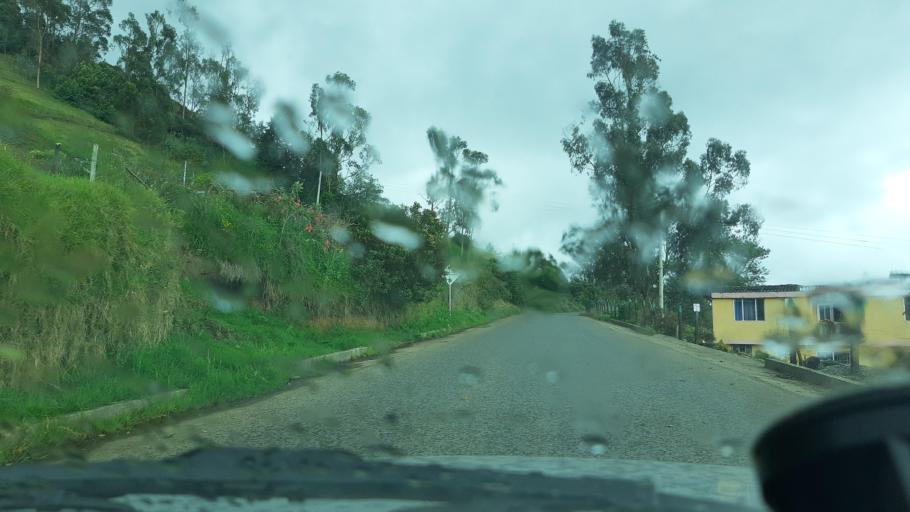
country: CO
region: Cundinamarca
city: Umbita
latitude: 5.2190
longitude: -73.4745
